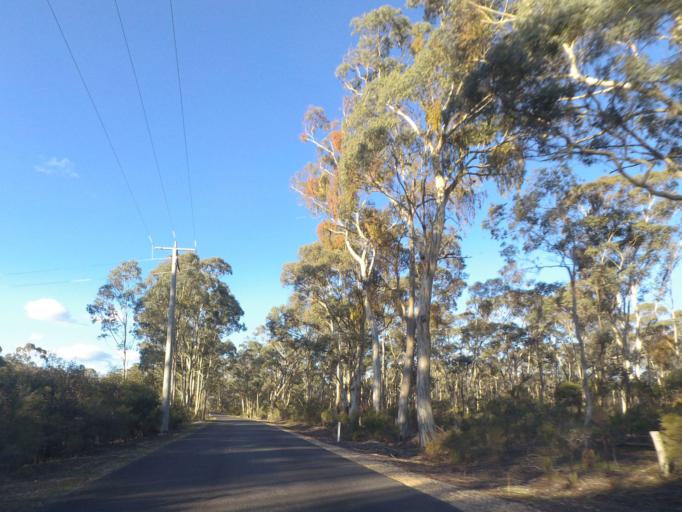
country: AU
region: Victoria
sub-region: Mount Alexander
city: Castlemaine
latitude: -37.1424
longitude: 144.1962
